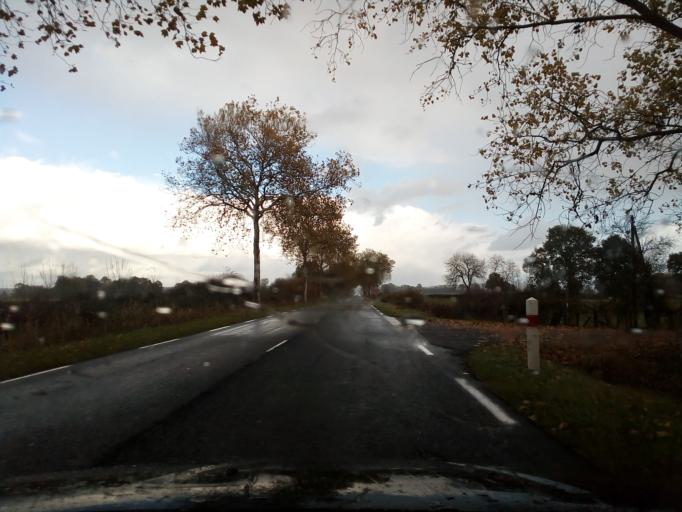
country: FR
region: Auvergne
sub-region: Departement de l'Allier
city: Saint-Pourcain-sur-Sioule
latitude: 46.3169
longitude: 3.3302
